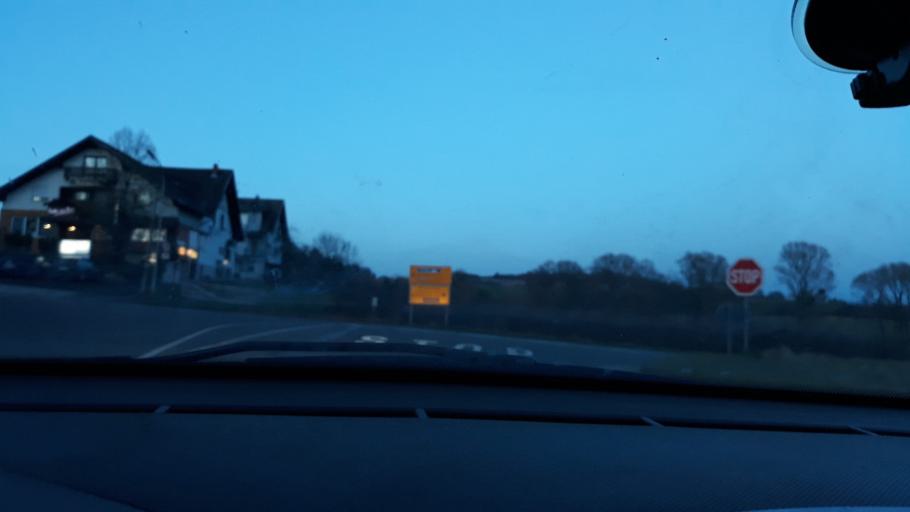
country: DE
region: Saarland
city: Kleinblittersdorf
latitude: 49.1580
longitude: 7.0898
